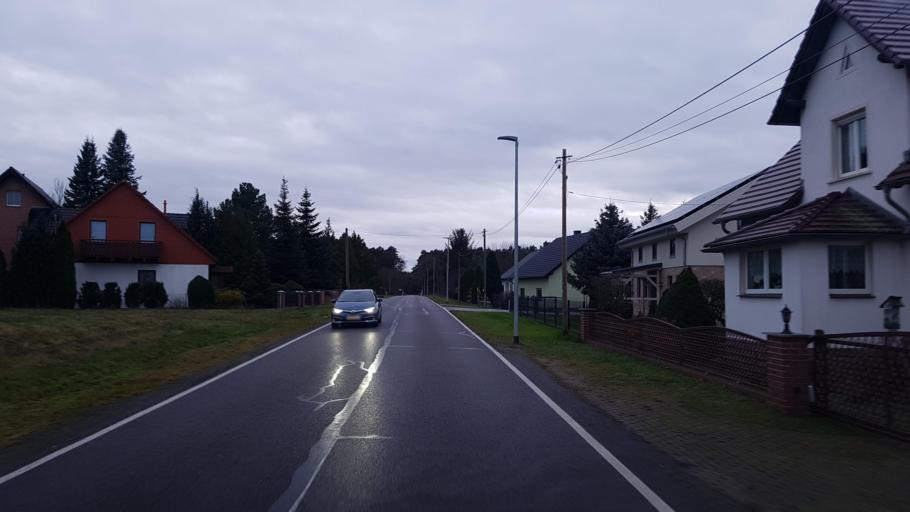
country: DE
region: Brandenburg
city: Schlepzig
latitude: 52.0219
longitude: 13.9809
